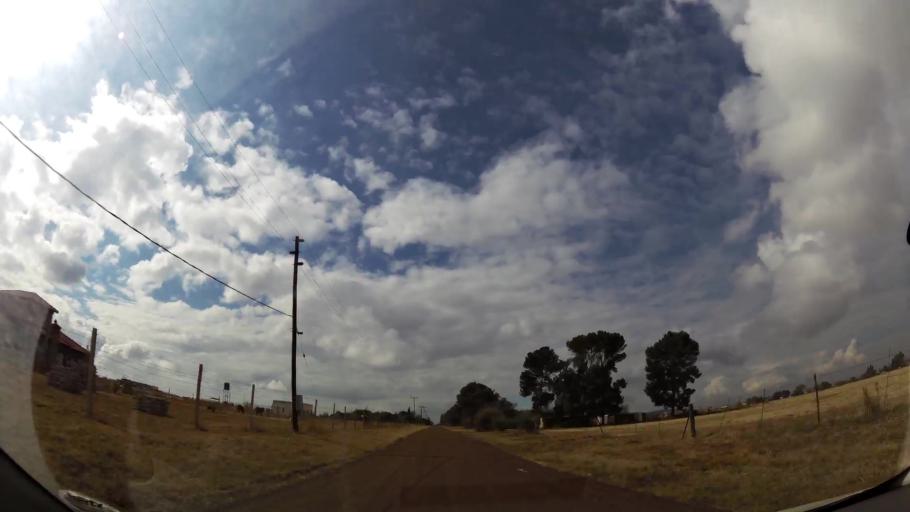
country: ZA
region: Gauteng
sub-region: Sedibeng District Municipality
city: Meyerton
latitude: -26.6207
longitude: 28.0749
